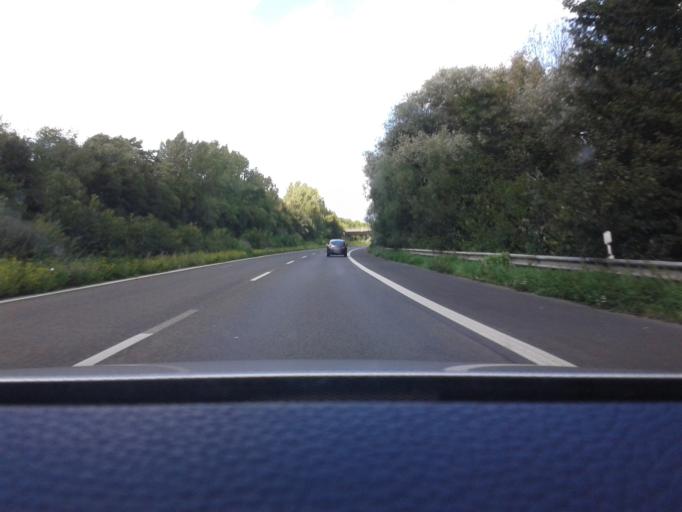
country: DE
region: North Rhine-Westphalia
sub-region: Regierungsbezirk Dusseldorf
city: Moers
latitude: 51.4297
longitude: 6.6731
